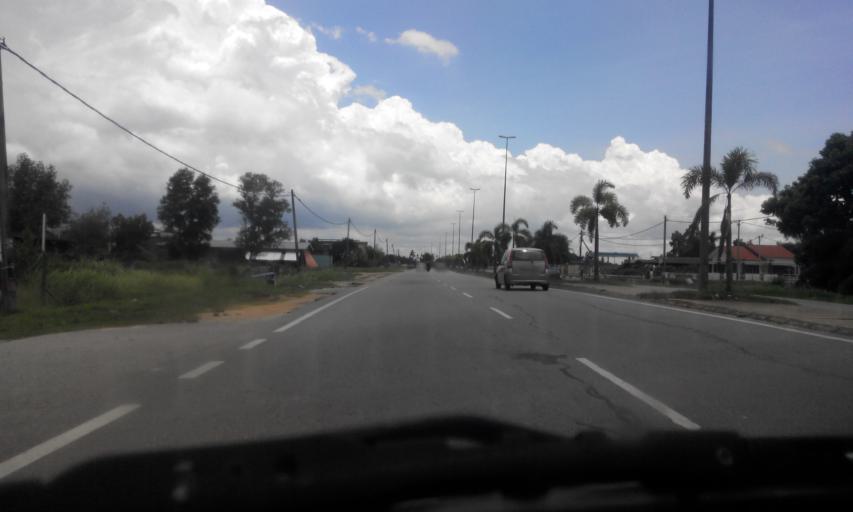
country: MY
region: Perak
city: Parit Buntar
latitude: 5.1301
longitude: 100.5000
